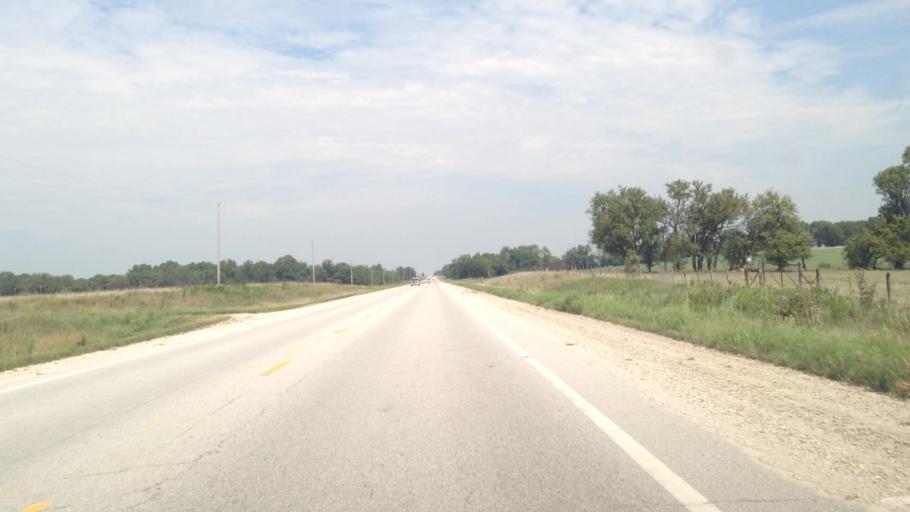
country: US
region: Kansas
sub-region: Neosho County
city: Erie
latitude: 37.4591
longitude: -95.2697
